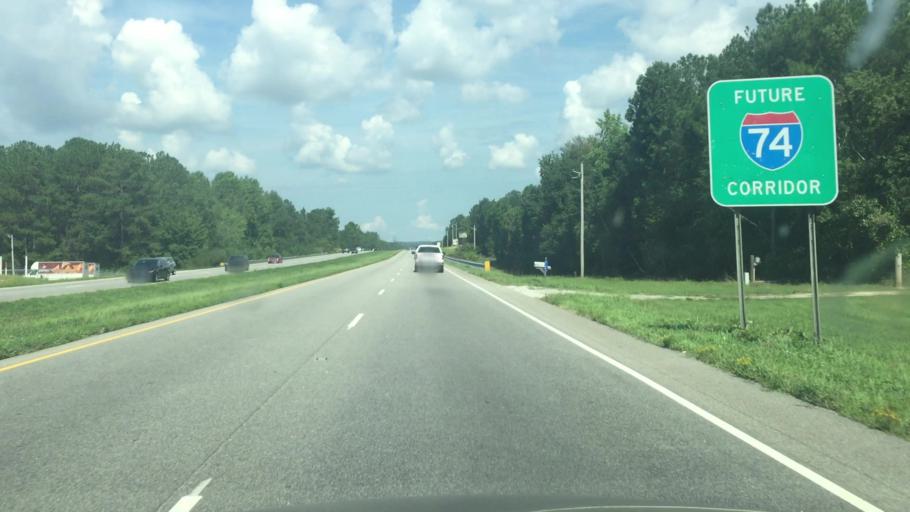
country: US
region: North Carolina
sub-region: Scotland County
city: Laurel Hill
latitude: 34.8391
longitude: -79.6007
